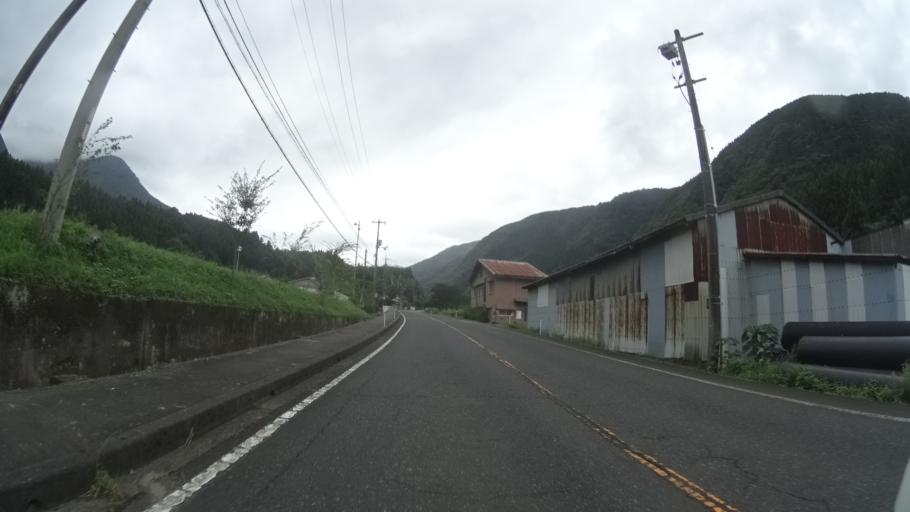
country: JP
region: Tottori
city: Kurayoshi
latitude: 35.4453
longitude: 134.0278
